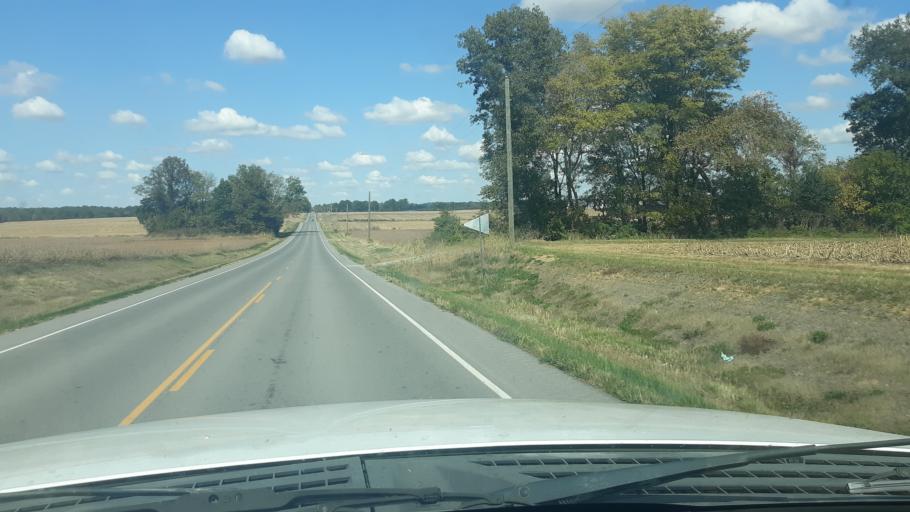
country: US
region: Illinois
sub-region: Saline County
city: Eldorado
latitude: 37.7967
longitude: -88.4848
